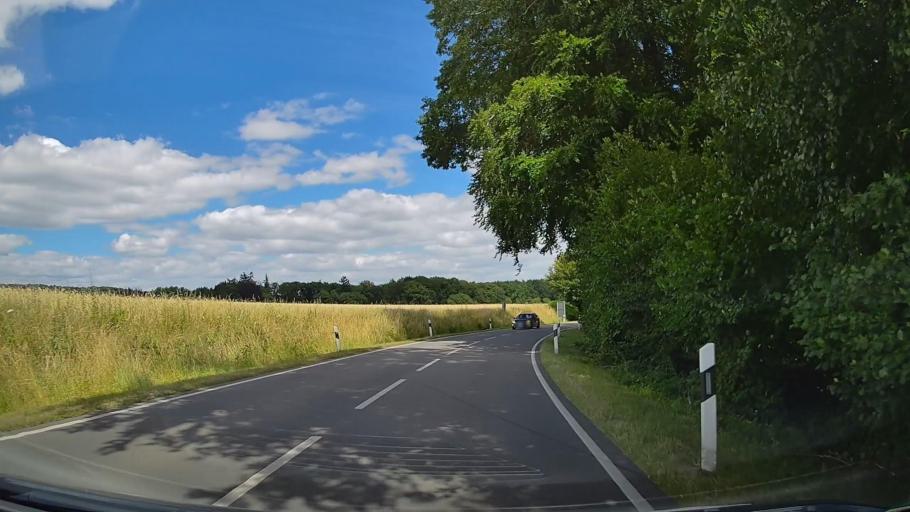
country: DE
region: Lower Saxony
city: Belm
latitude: 52.3658
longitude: 8.1446
